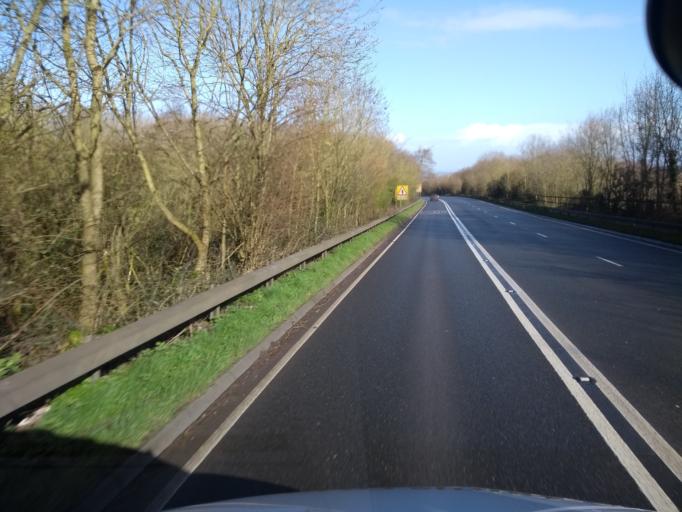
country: GB
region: England
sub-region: Somerset
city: Yeovil
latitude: 50.9619
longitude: -2.6522
